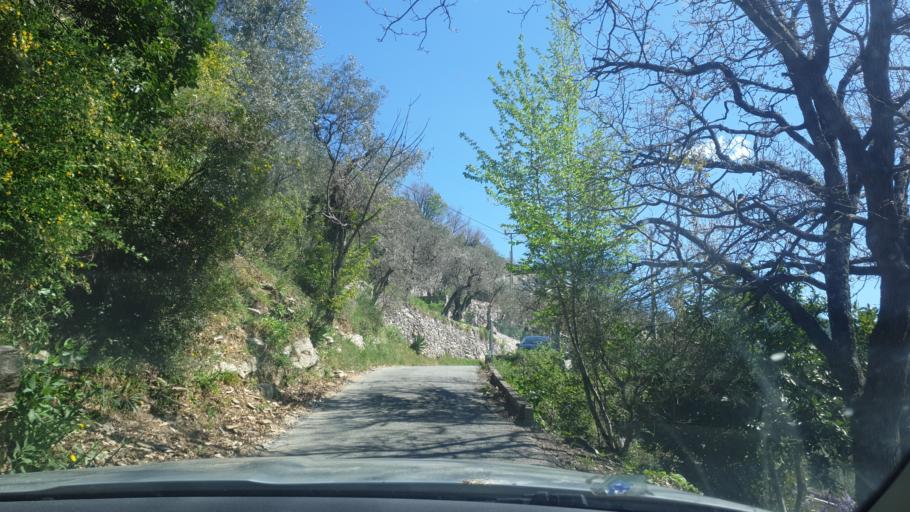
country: IT
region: Liguria
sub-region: Provincia di Genova
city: Avegno
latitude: 44.3787
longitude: 9.1470
